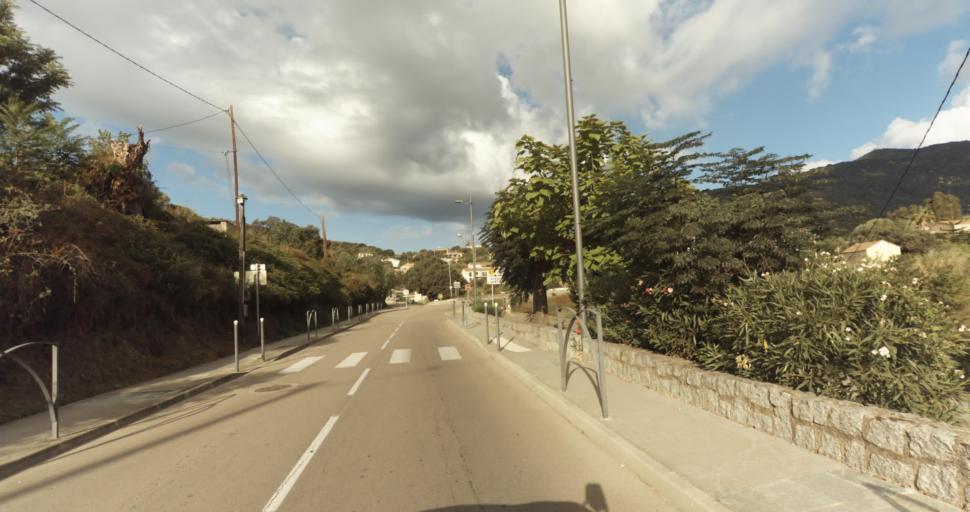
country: FR
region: Corsica
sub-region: Departement de la Corse-du-Sud
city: Ajaccio
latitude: 41.9292
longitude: 8.7274
